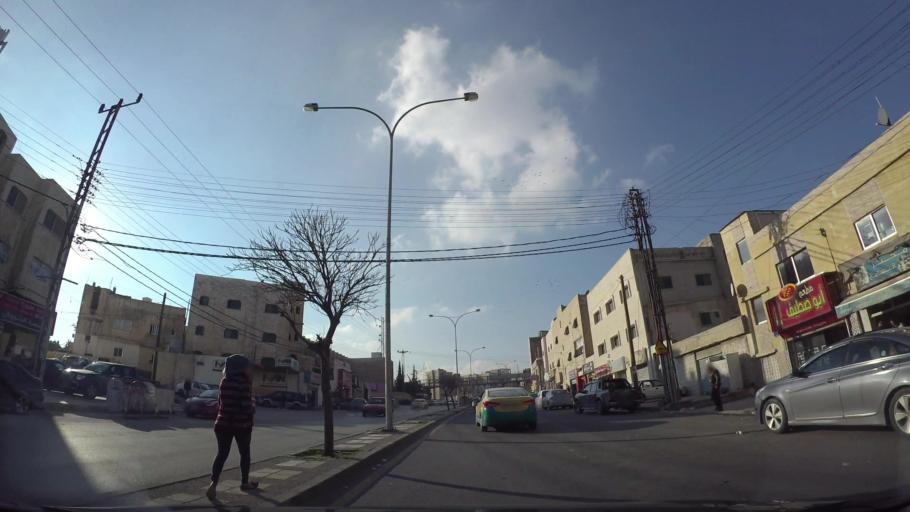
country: JO
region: Amman
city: Amman
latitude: 31.9770
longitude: 35.9448
